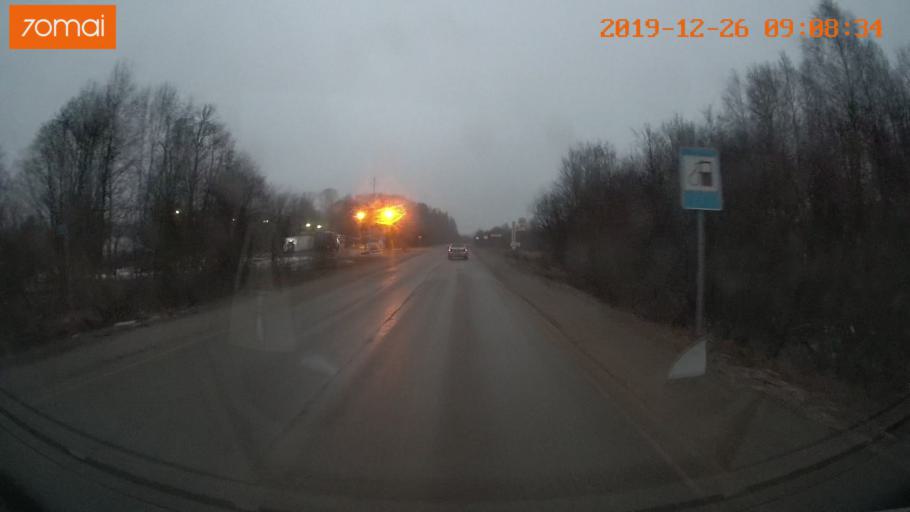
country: RU
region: Vologda
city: Gryazovets
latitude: 58.8581
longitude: 40.2487
